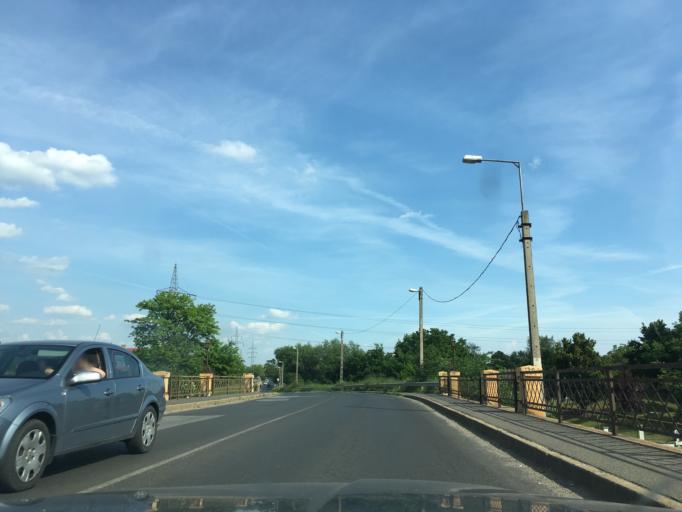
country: HU
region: Hajdu-Bihar
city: Debrecen
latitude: 47.5249
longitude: 21.6411
